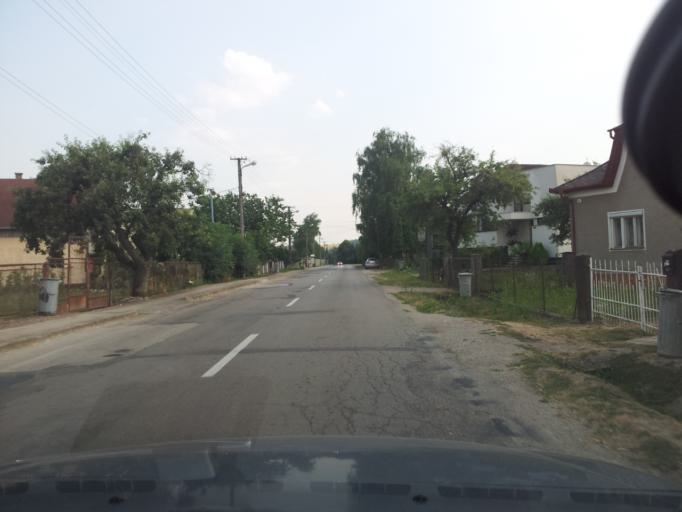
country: SK
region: Nitriansky
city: Banovce nad Bebravou
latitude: 48.7830
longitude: 18.1978
